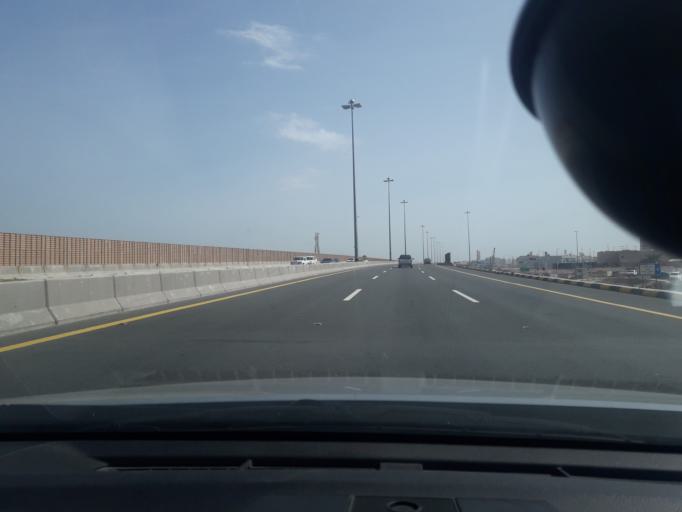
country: SA
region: Al Madinah al Munawwarah
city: Medina
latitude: 24.4440
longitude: 39.6385
